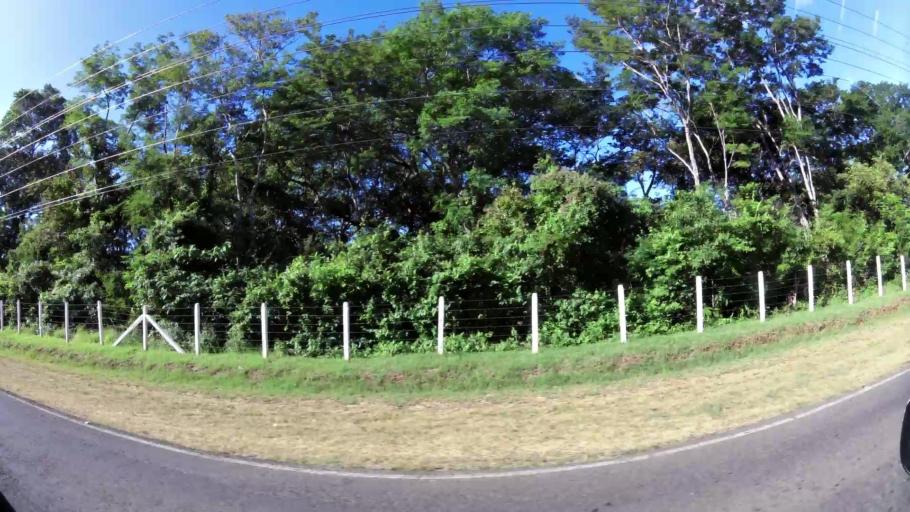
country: CR
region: Guanacaste
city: Sardinal
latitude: 10.3838
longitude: -85.7890
